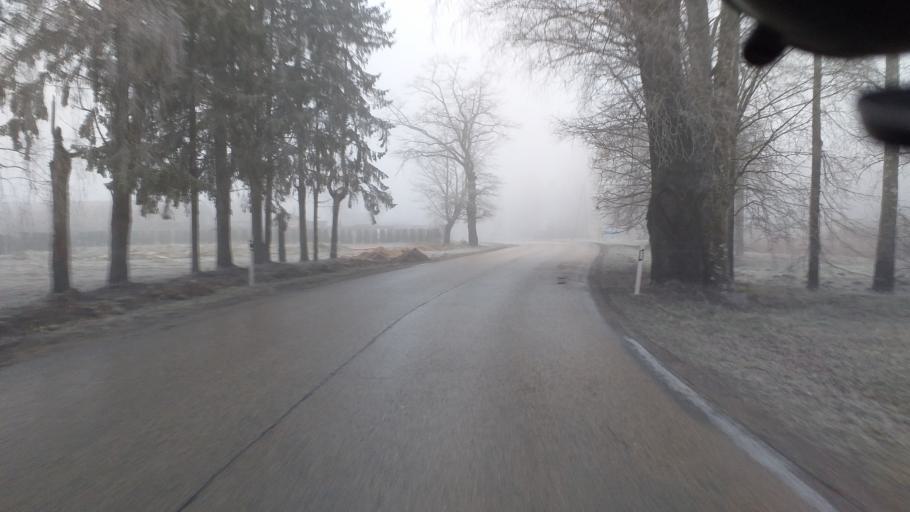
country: LV
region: Olaine
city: Olaine
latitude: 56.7942
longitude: 23.9413
